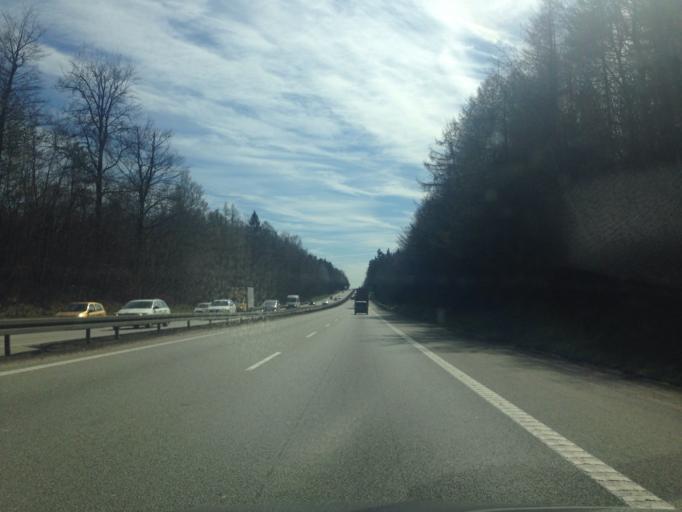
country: PL
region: Pomeranian Voivodeship
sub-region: Gdynia
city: Wielki Kack
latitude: 54.4480
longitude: 18.4921
